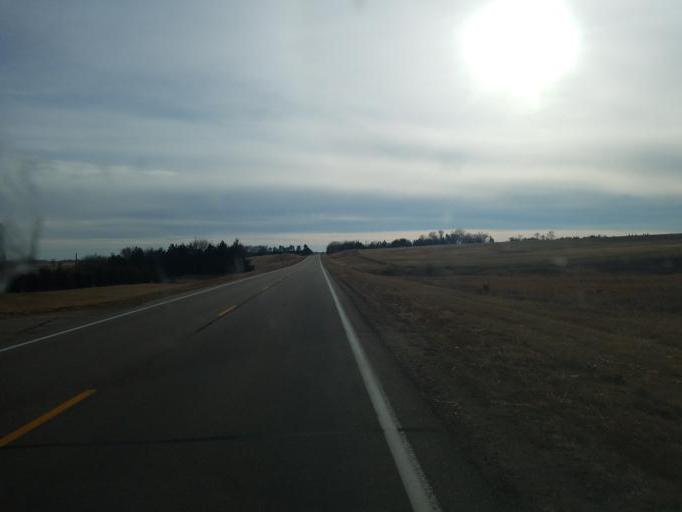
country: US
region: Nebraska
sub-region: Knox County
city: Creighton
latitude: 42.4517
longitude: -97.8967
